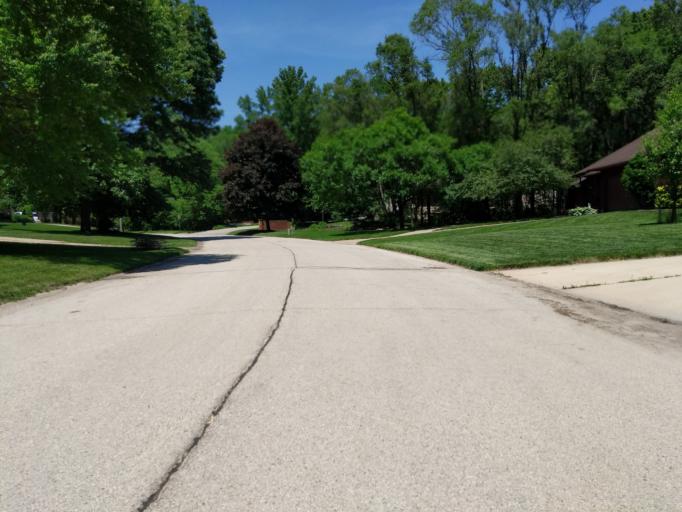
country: US
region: Iowa
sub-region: Linn County
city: Cedar Rapids
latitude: 42.0183
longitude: -91.6243
